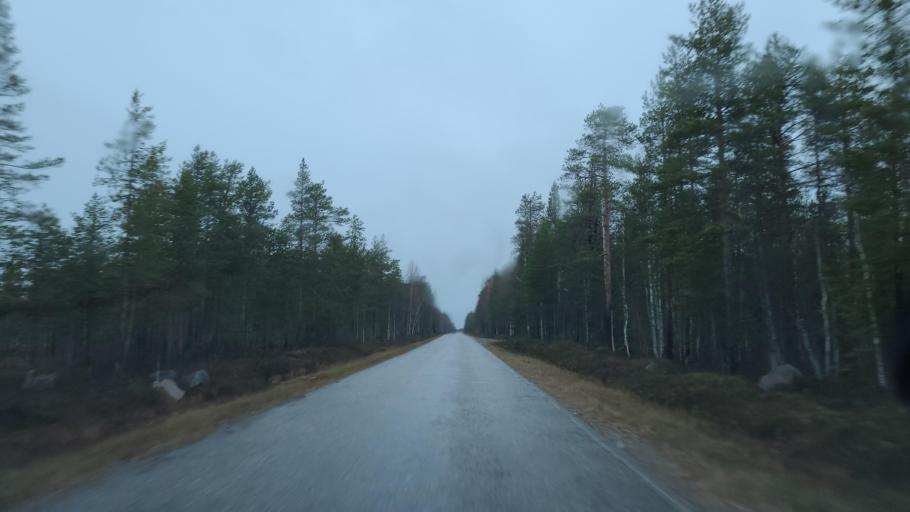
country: FI
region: Lapland
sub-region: Kemi-Tornio
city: Simo
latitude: 65.8689
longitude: 25.2231
